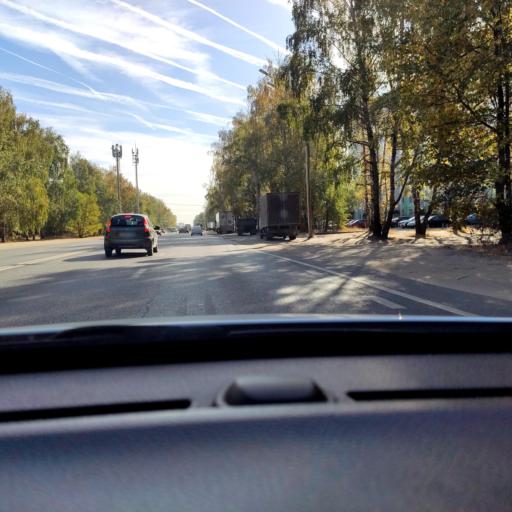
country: RU
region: Voronezj
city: Pridonskoy
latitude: 51.6886
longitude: 39.1057
